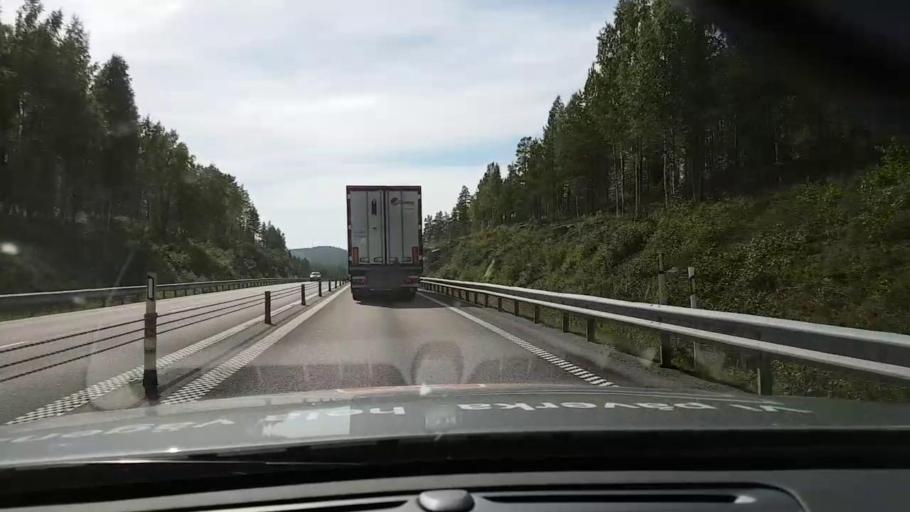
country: SE
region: Vaesternorrland
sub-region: OErnskoeldsviks Kommun
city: Husum
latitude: 63.4669
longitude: 19.2712
